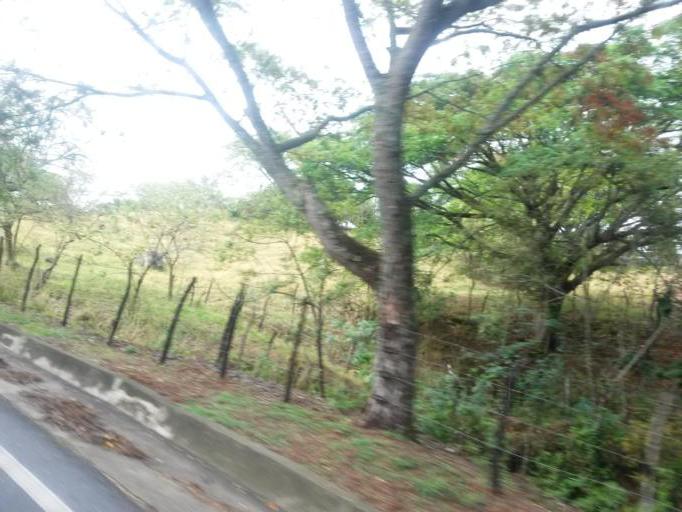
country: CO
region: Cauca
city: El Bordo
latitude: 2.1734
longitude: -76.8973
